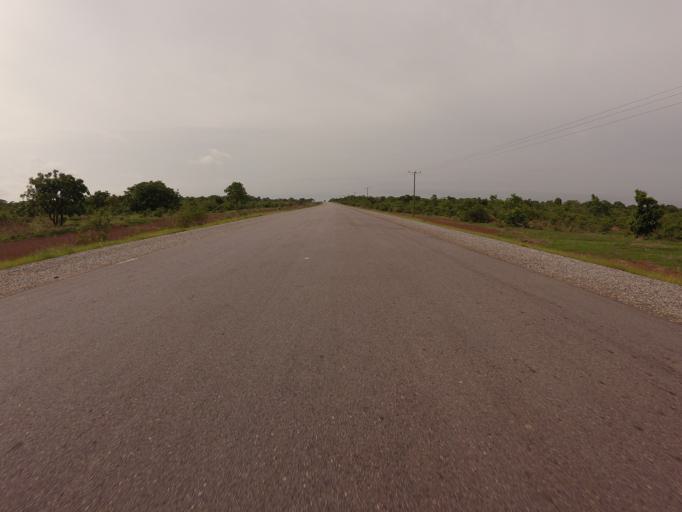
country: GH
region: Northern
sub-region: Yendi
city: Yendi
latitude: 9.6189
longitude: -0.0502
